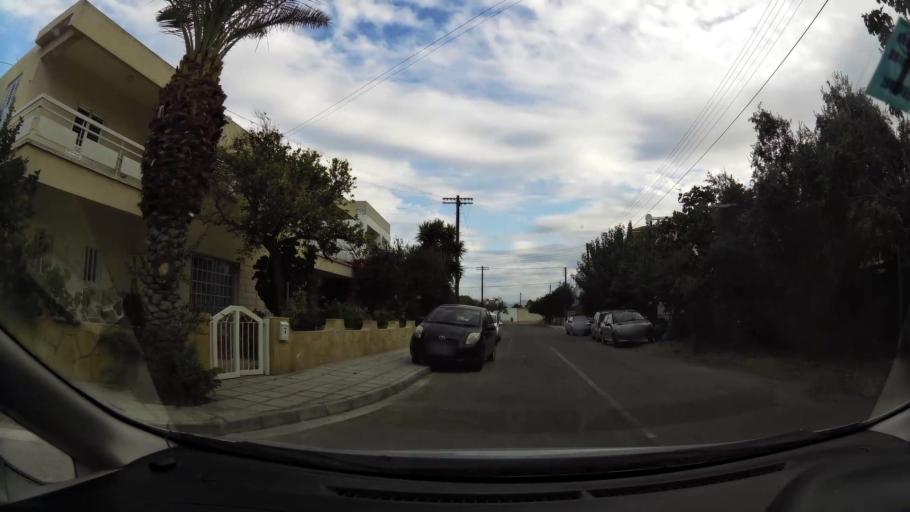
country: CY
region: Lefkosia
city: Nicosia
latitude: 35.1420
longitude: 33.3357
